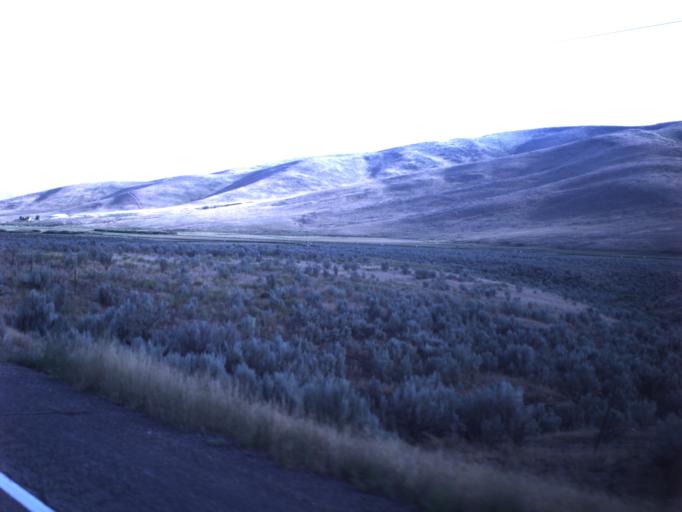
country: US
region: Utah
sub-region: Utah County
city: Woodland Hills
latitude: 39.8397
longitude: -111.5134
